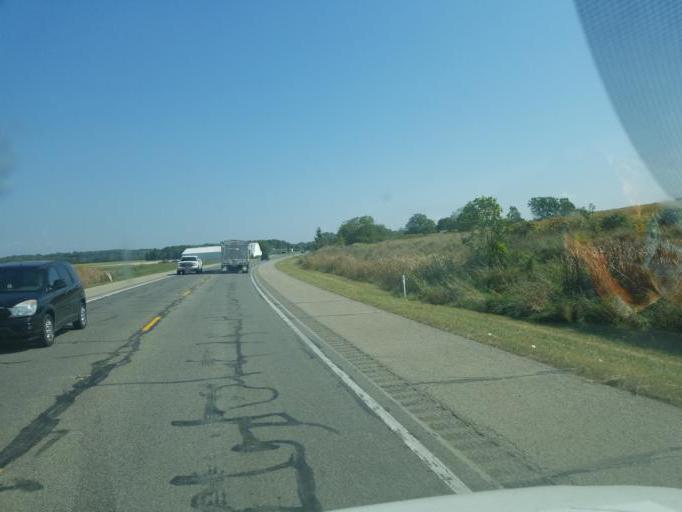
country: US
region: Indiana
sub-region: Steuben County
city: Angola
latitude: 41.6344
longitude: -85.0918
